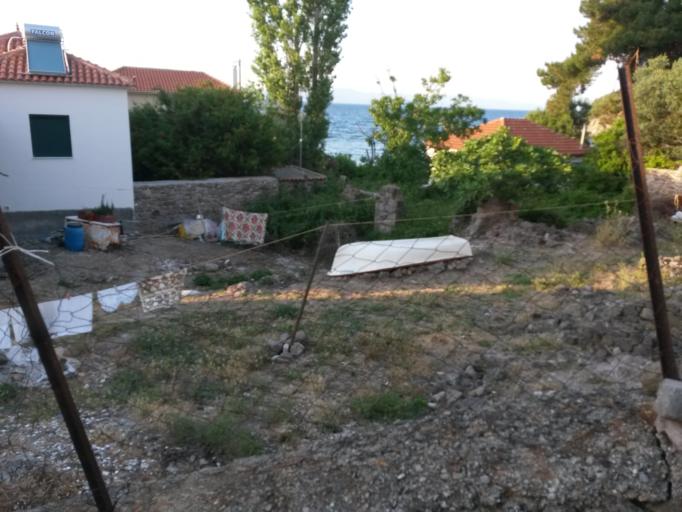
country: GR
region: North Aegean
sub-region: Nomos Lesvou
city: Mantamados
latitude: 39.3732
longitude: 26.3036
